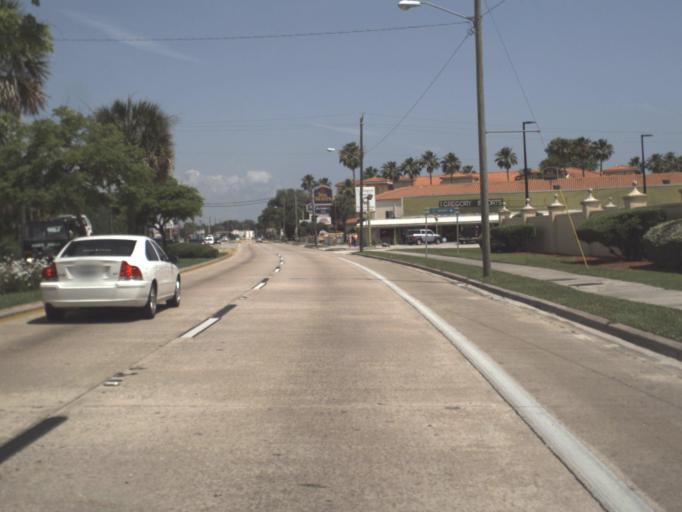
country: US
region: Florida
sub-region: Saint Johns County
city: Saint Augustine
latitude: 29.9101
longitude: -81.3218
